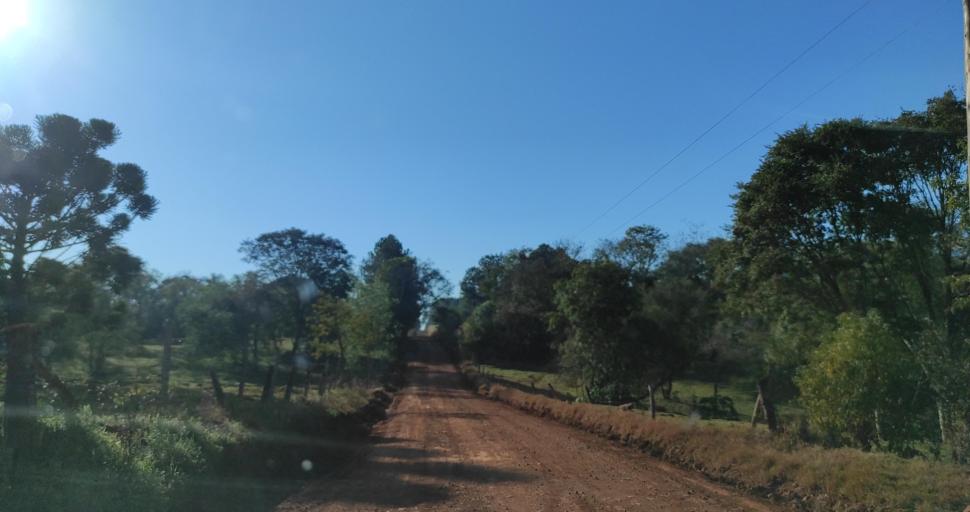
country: AR
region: Misiones
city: Capiovi
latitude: -26.8801
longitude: -55.0196
